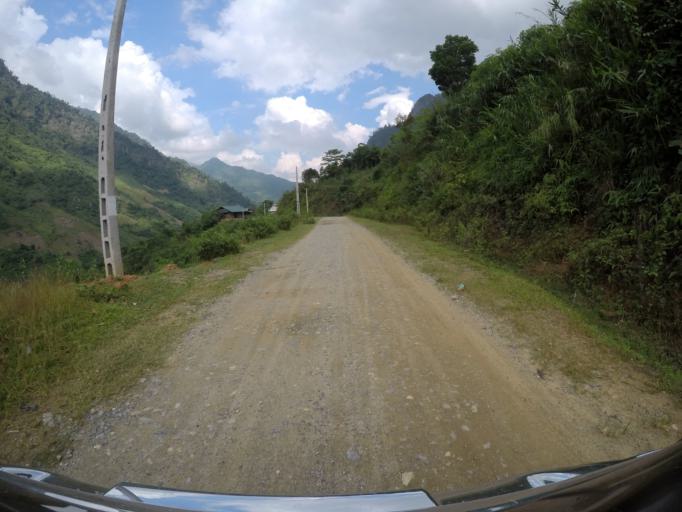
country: VN
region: Yen Bai
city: Son Thinh
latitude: 21.6803
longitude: 104.5559
